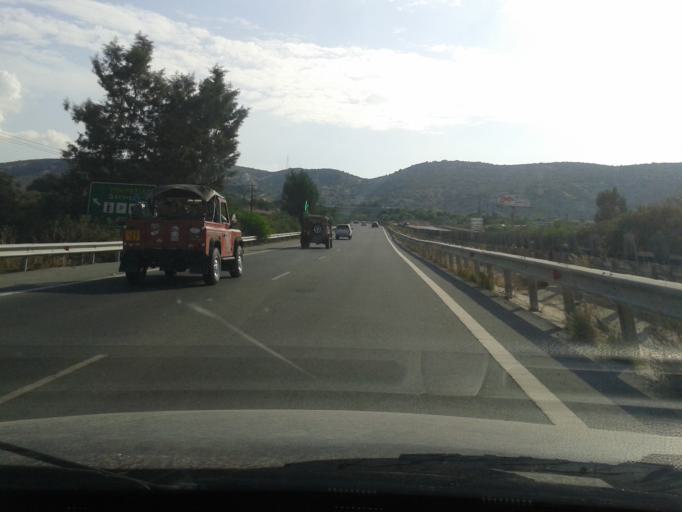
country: CY
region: Limassol
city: Pyrgos
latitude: 34.7219
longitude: 33.1989
